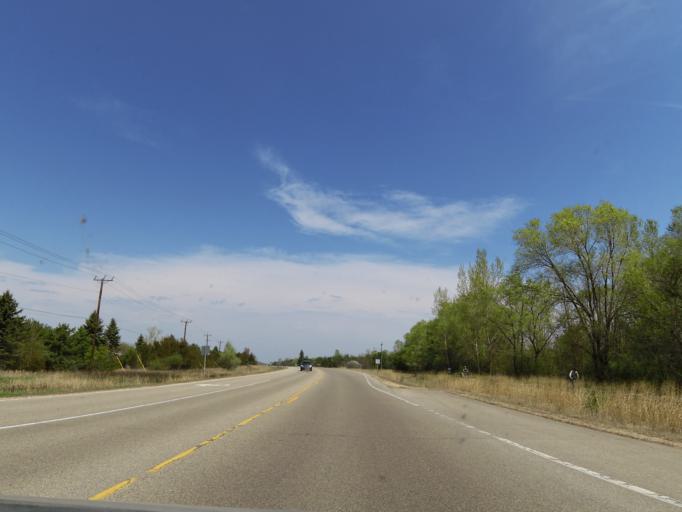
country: US
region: Minnesota
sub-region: Washington County
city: Lake Saint Croix Beach
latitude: 44.9276
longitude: -92.7713
